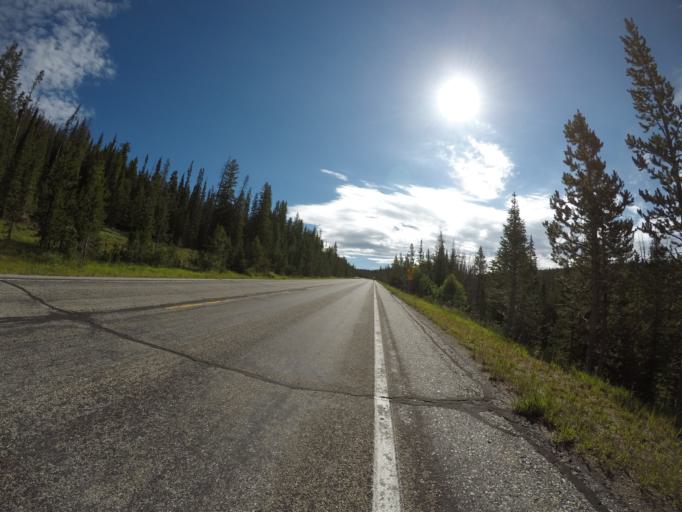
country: US
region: Wyoming
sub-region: Carbon County
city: Saratoga
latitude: 41.3234
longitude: -106.4517
